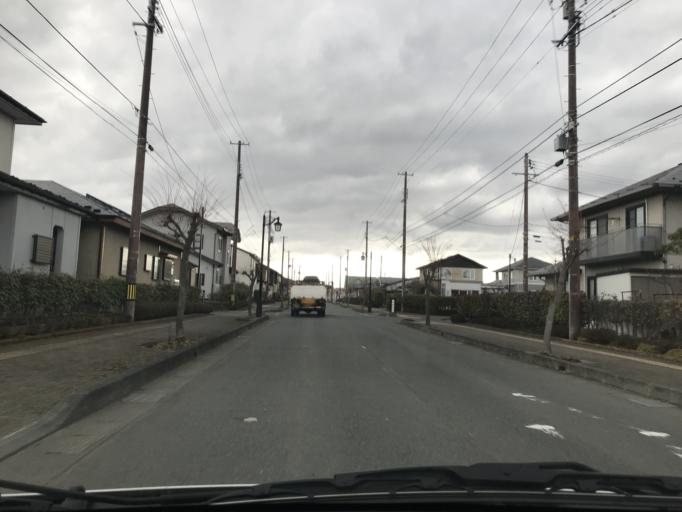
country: JP
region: Iwate
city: Mizusawa
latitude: 39.1148
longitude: 141.1644
